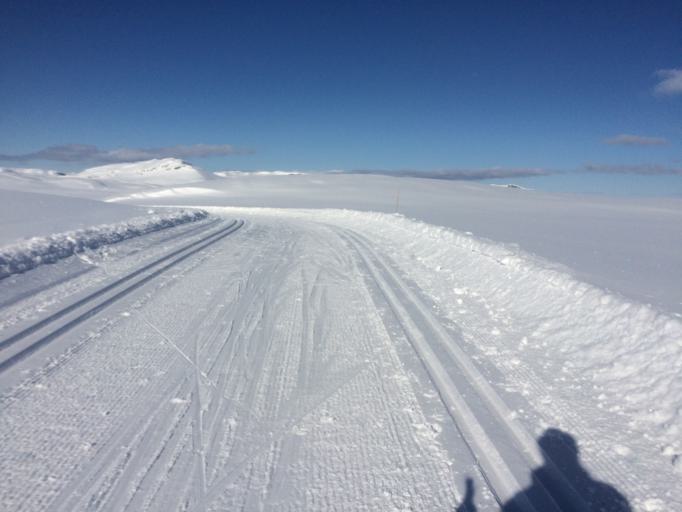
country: NO
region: Oppland
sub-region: Ringebu
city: Ringebu
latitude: 61.3553
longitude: 10.0872
